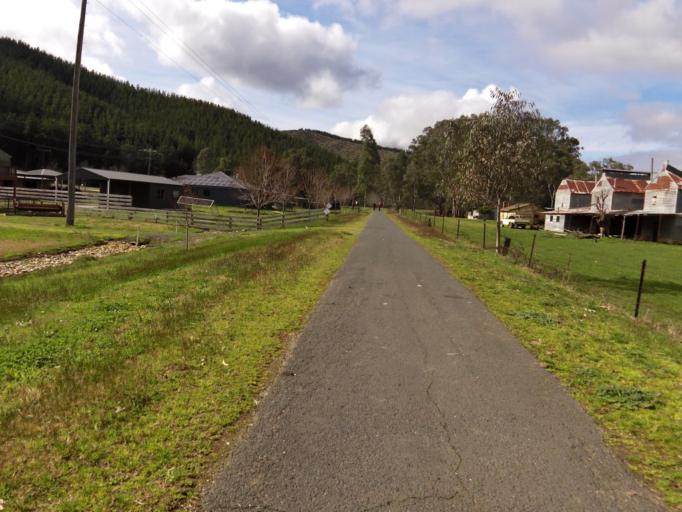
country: AU
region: Victoria
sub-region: Alpine
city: Mount Beauty
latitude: -36.5747
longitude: 146.7442
